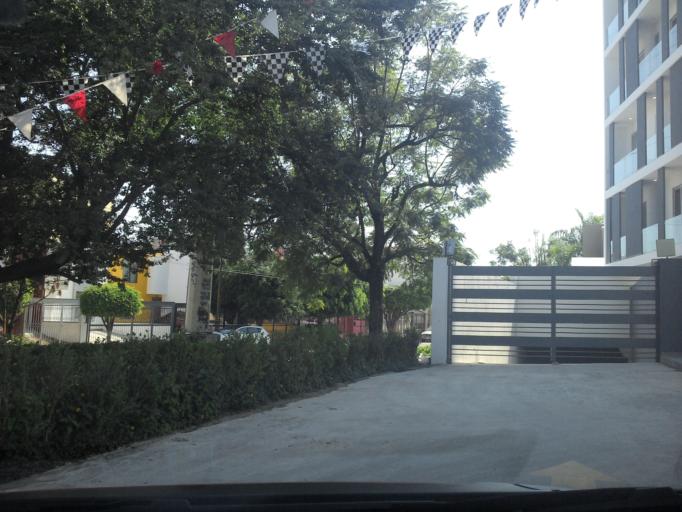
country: MX
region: Jalisco
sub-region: Tlajomulco de Zuniga
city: Palomar
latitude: 20.6307
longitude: -103.4346
